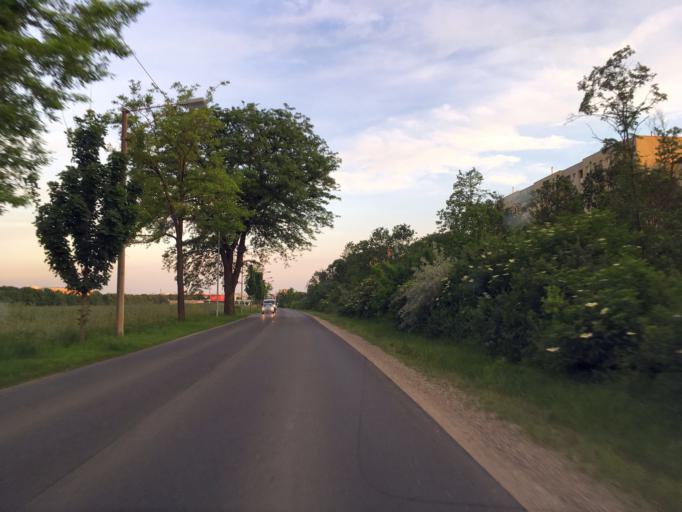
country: AT
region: Lower Austria
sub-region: Politischer Bezirk Wien-Umgebung
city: Gerasdorf bei Wien
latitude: 48.2727
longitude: 16.4570
